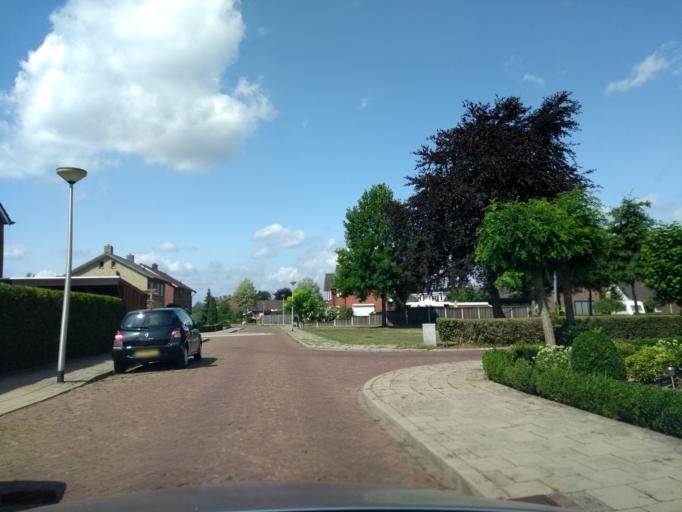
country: DE
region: Lower Saxony
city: Nordhorn
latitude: 52.3757
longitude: 7.0154
